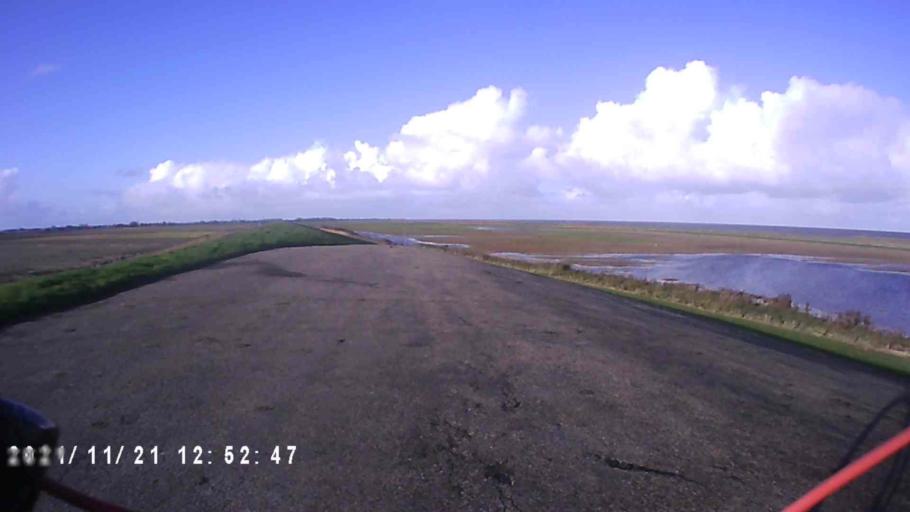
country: NL
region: Friesland
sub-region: Gemeente Dongeradeel
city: Anjum
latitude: 53.4014
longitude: 6.1289
